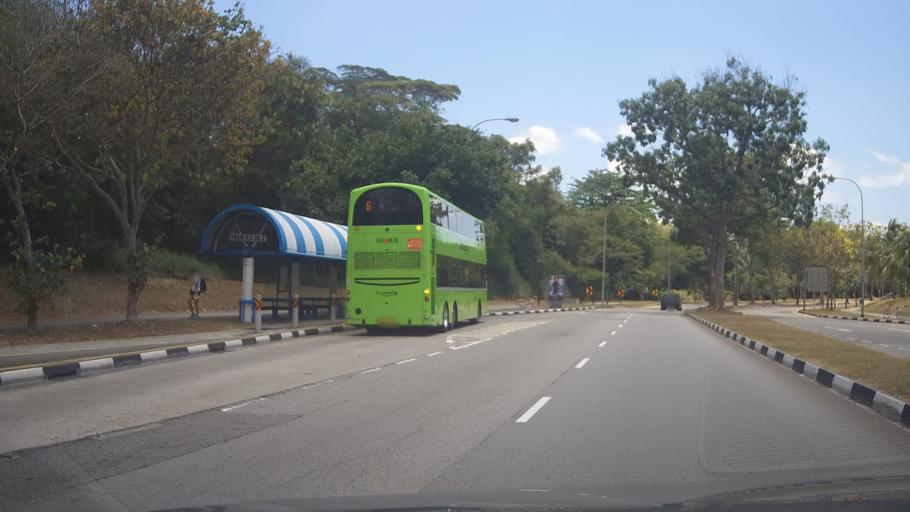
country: MY
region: Johor
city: Kampung Pasir Gudang Baru
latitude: 1.3751
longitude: 103.9618
